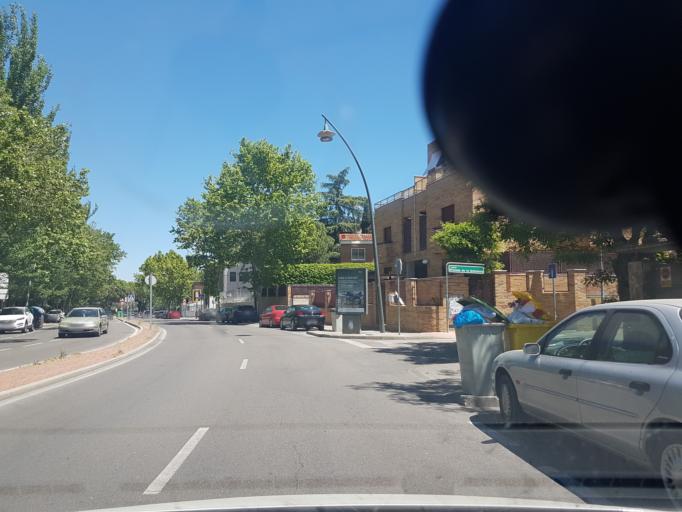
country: ES
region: Madrid
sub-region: Provincia de Madrid
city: Pozuelo de Alarcon
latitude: 40.4416
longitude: -3.8140
